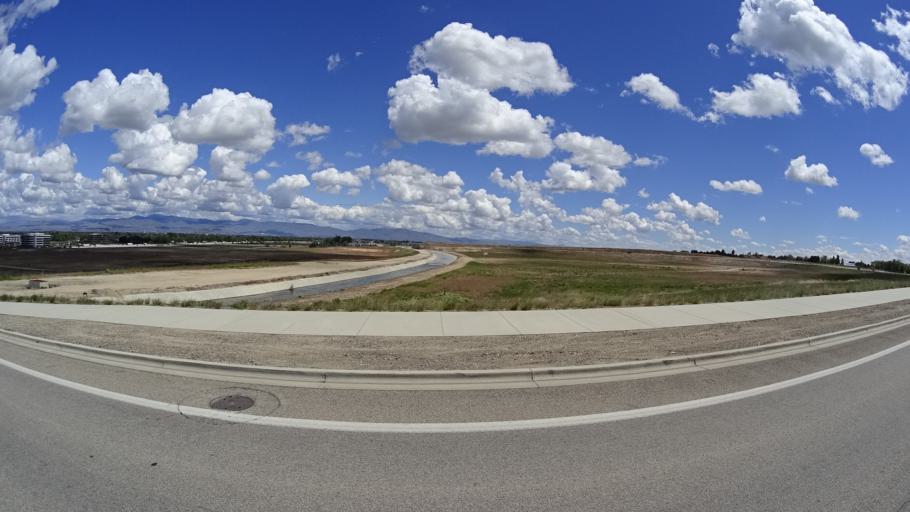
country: US
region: Idaho
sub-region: Ada County
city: Meridian
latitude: 43.5878
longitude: -116.4338
